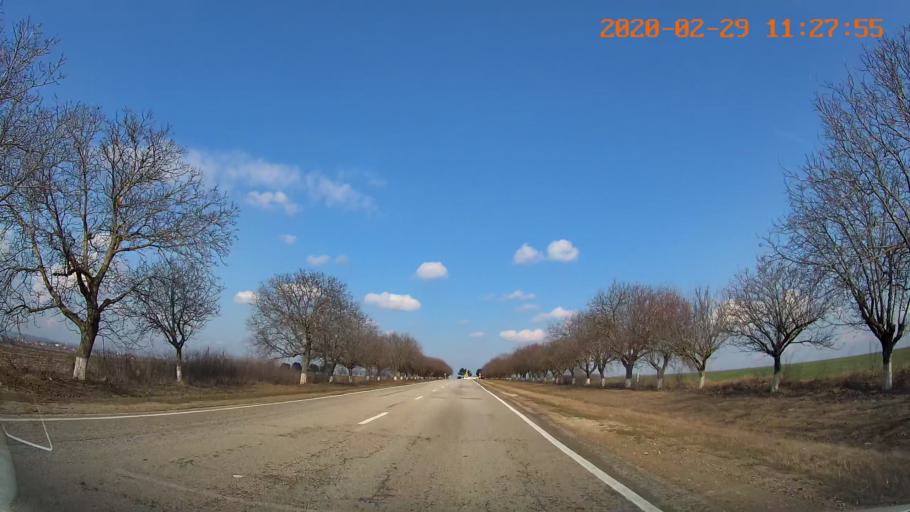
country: MD
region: Telenesti
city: Cocieri
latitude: 47.4757
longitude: 29.1405
